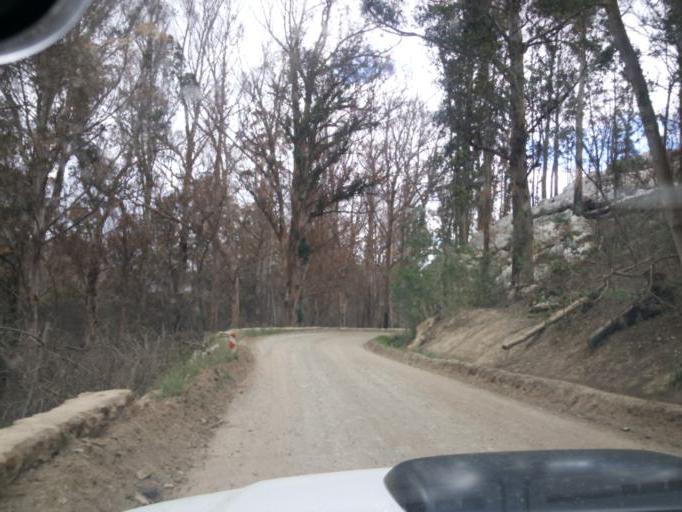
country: ZA
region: Western Cape
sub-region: Eden District Municipality
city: George
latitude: -33.8494
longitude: 22.4473
